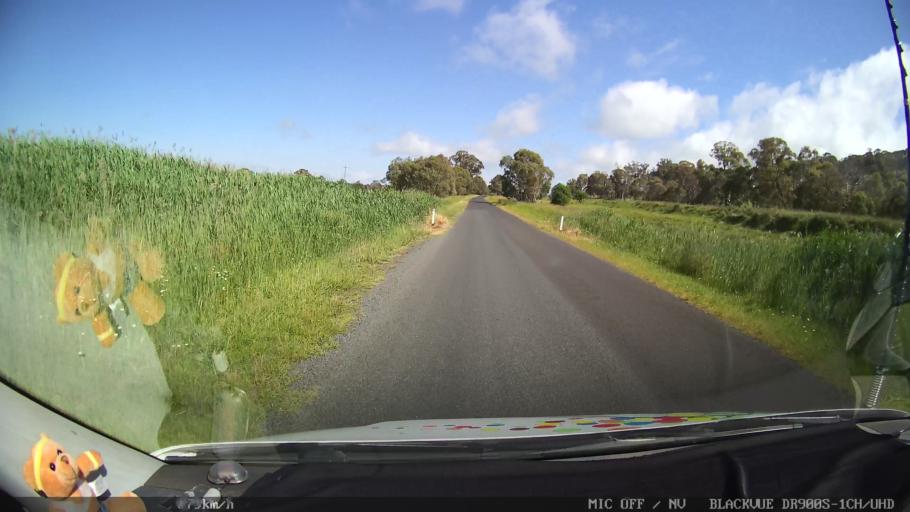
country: AU
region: New South Wales
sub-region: Guyra
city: Guyra
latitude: -30.0321
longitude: 151.6642
